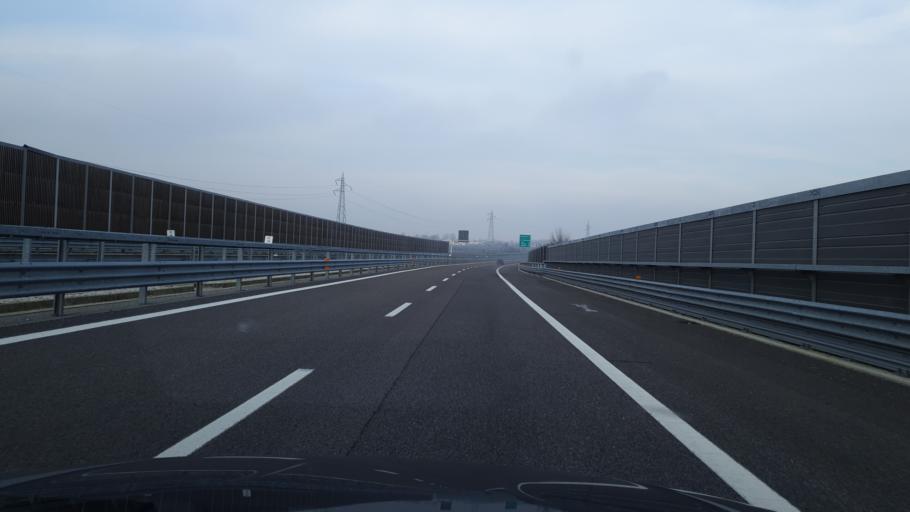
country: IT
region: Veneto
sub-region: Provincia di Padova
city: Saletto
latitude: 45.2265
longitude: 11.5512
